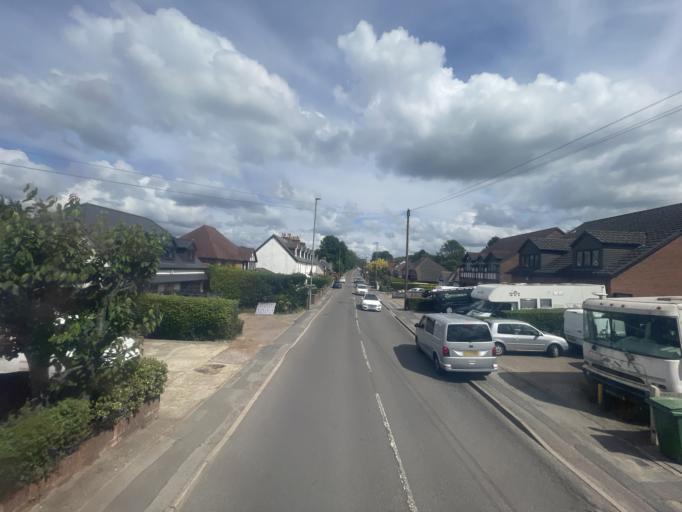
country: GB
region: England
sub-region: Kent
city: Biggin Hill
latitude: 51.3072
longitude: 0.0443
